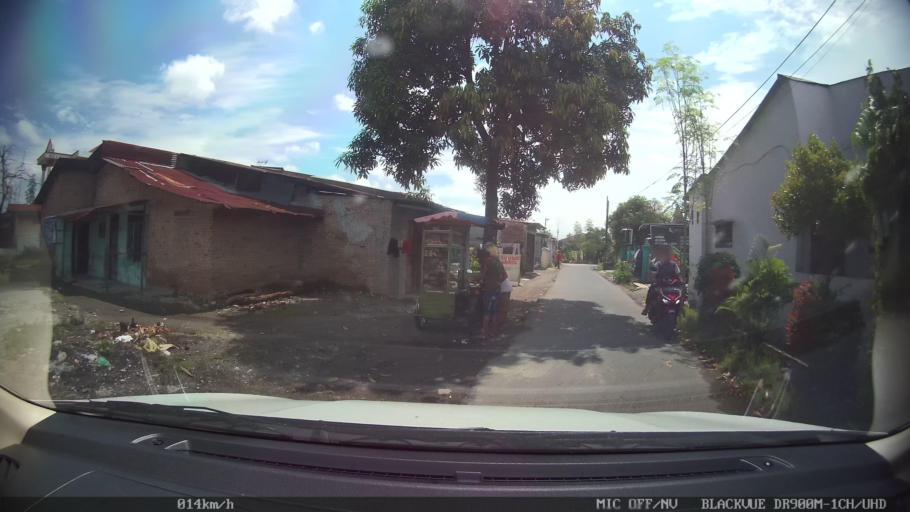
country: ID
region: North Sumatra
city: Medan
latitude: 3.6023
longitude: 98.7490
